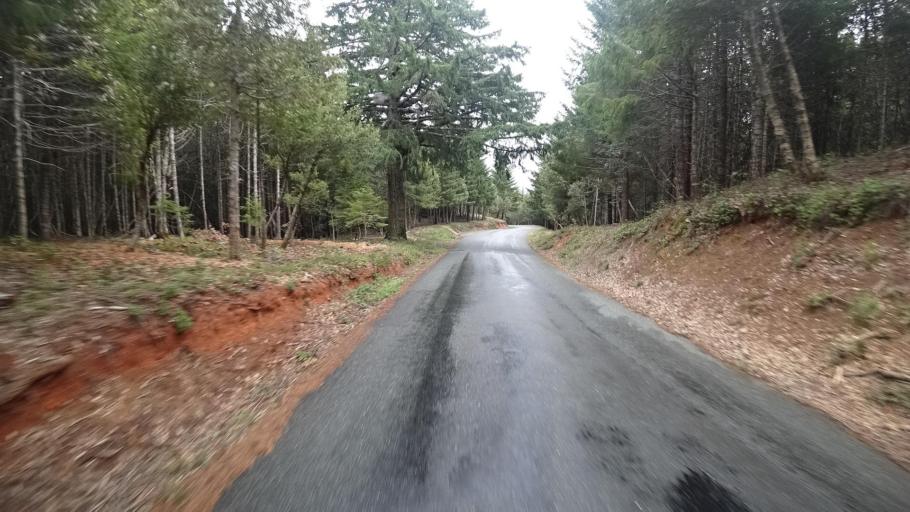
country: US
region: California
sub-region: Humboldt County
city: Willow Creek
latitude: 41.2018
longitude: -123.7962
